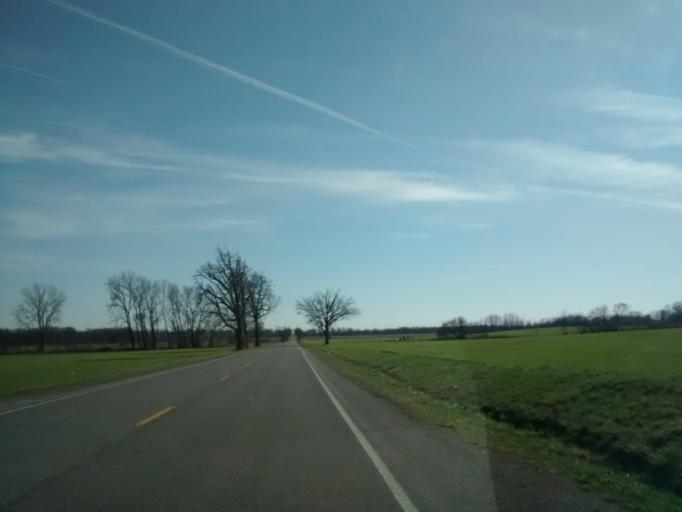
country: US
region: New York
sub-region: Livingston County
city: Avon
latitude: 42.9431
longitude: -77.7736
